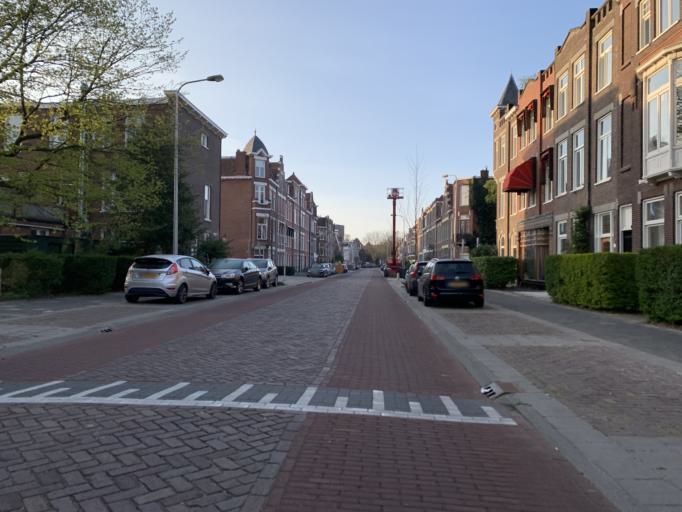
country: NL
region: Groningen
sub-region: Gemeente Groningen
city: Groningen
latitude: 53.2187
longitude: 6.5489
